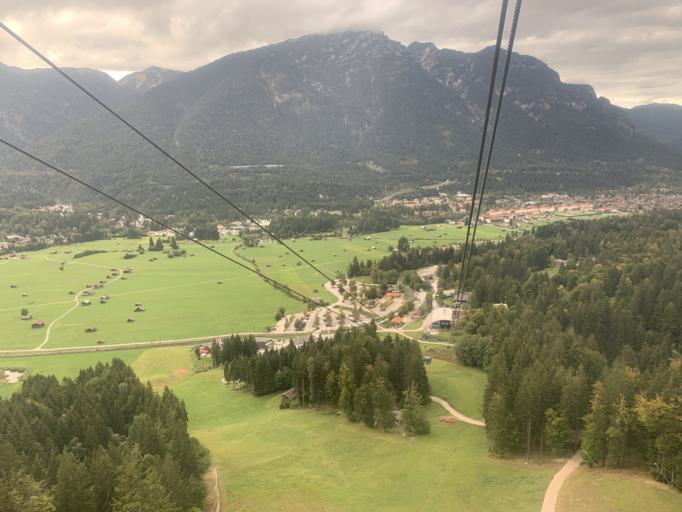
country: DE
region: Bavaria
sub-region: Upper Bavaria
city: Garmisch-Partenkirchen
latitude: 47.4667
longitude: 11.0646
